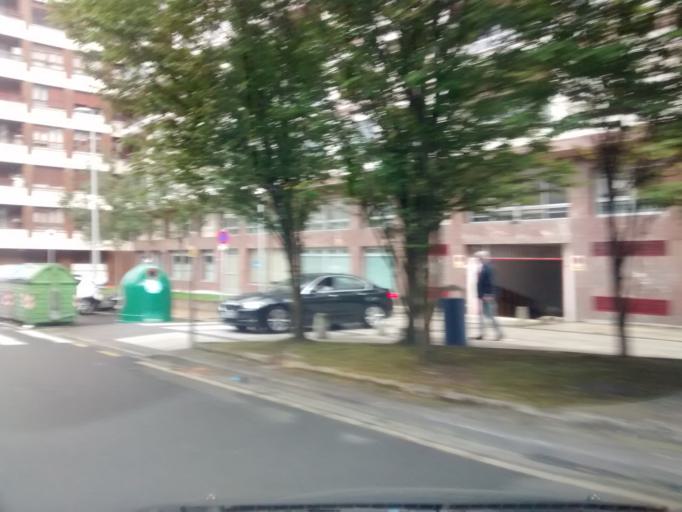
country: ES
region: Basque Country
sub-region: Provincia de Guipuzcoa
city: San Sebastian
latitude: 43.3057
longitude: -1.9826
